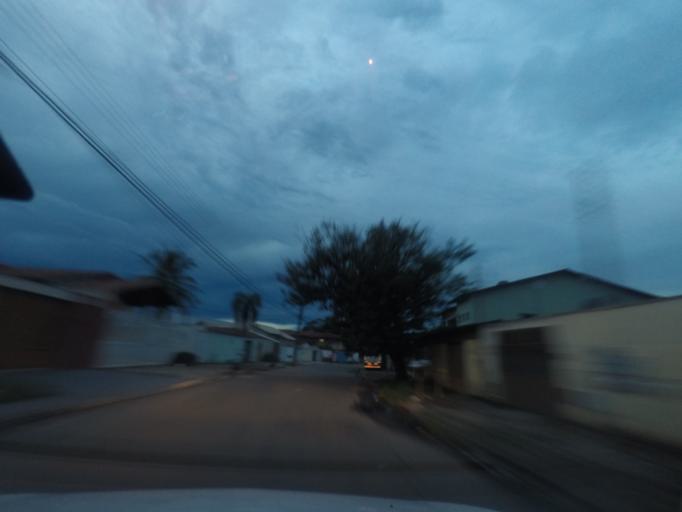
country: BR
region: Goias
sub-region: Goiania
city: Goiania
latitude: -16.7169
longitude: -49.3055
